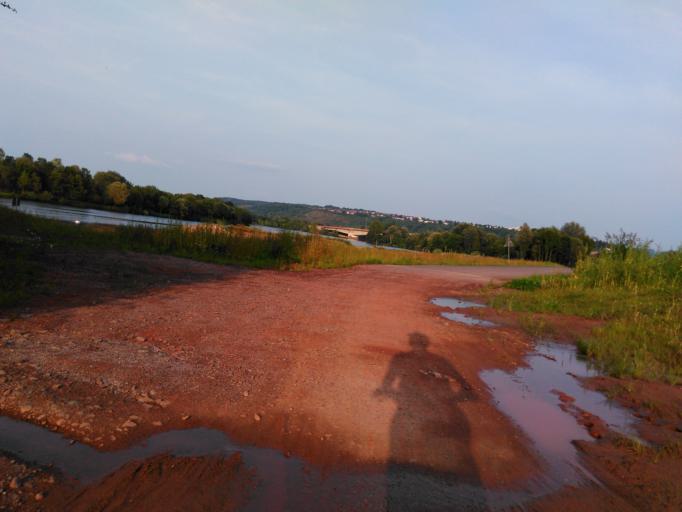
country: DE
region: Rheinland-Pfalz
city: Konz
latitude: 49.7003
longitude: 6.5590
